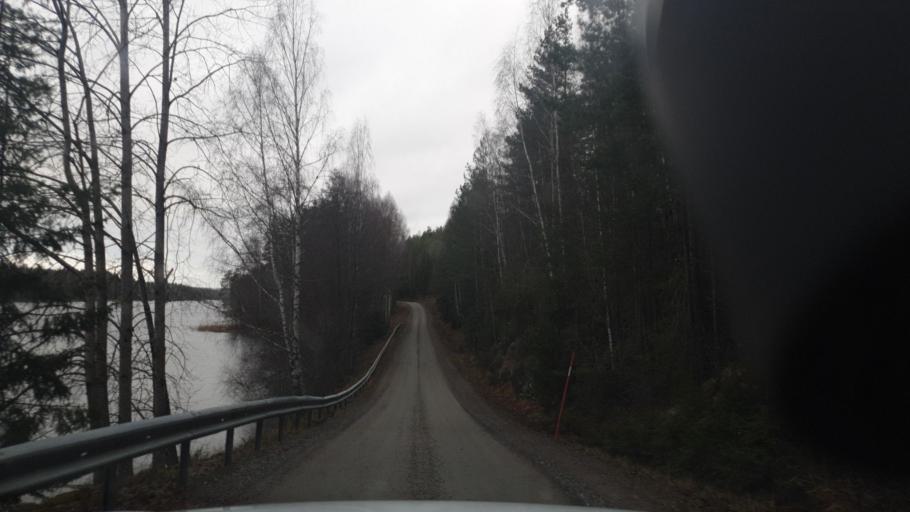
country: SE
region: Vaermland
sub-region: Sunne Kommun
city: Sunne
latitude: 59.6328
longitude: 13.0629
